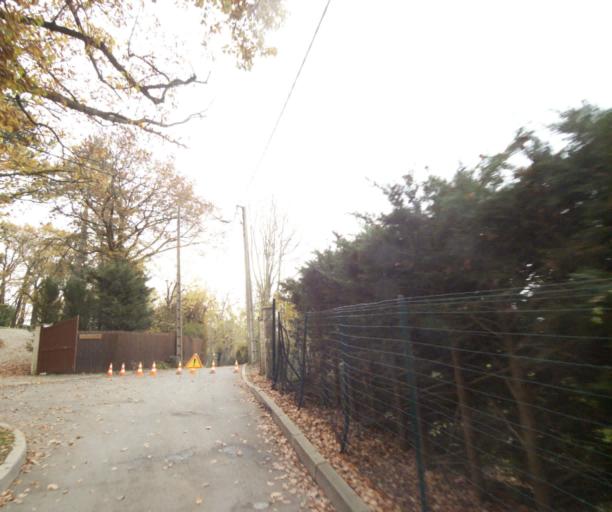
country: FR
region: Ile-de-France
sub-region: Departement des Yvelines
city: Triel-sur-Seine
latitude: 48.9907
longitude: 1.9987
